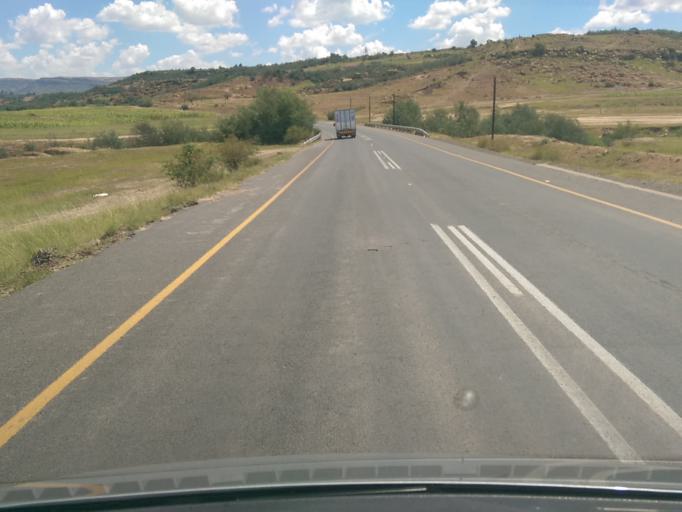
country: LS
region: Maseru
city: Maseru
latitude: -29.3926
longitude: 27.5451
